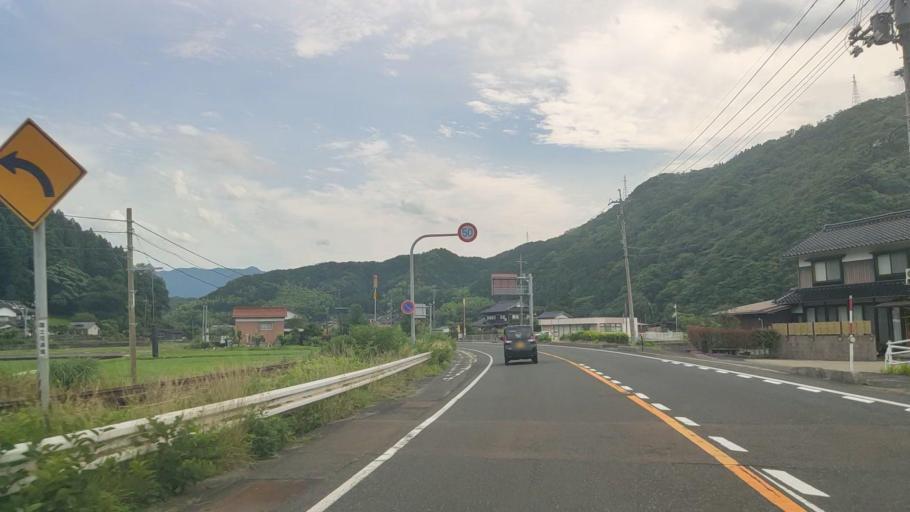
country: JP
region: Tottori
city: Tottori
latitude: 35.3529
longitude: 134.2048
